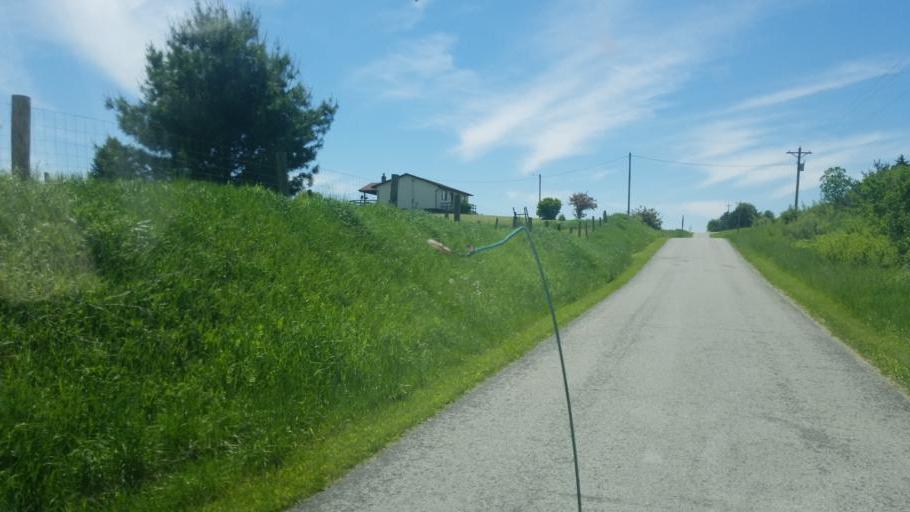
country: US
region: Ohio
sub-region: Huron County
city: Willard
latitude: 41.1202
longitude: -82.6958
